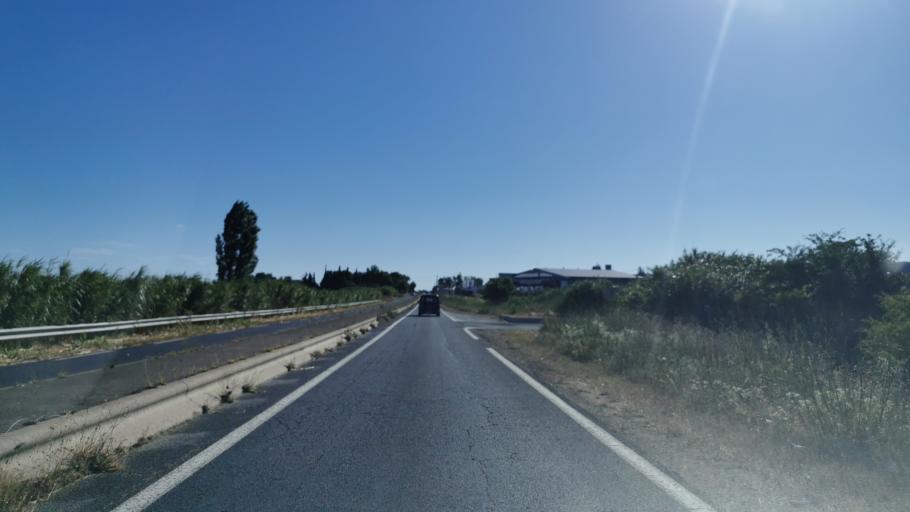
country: FR
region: Languedoc-Roussillon
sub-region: Departement de l'Herault
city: Colombiers
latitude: 43.3049
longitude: 3.1604
